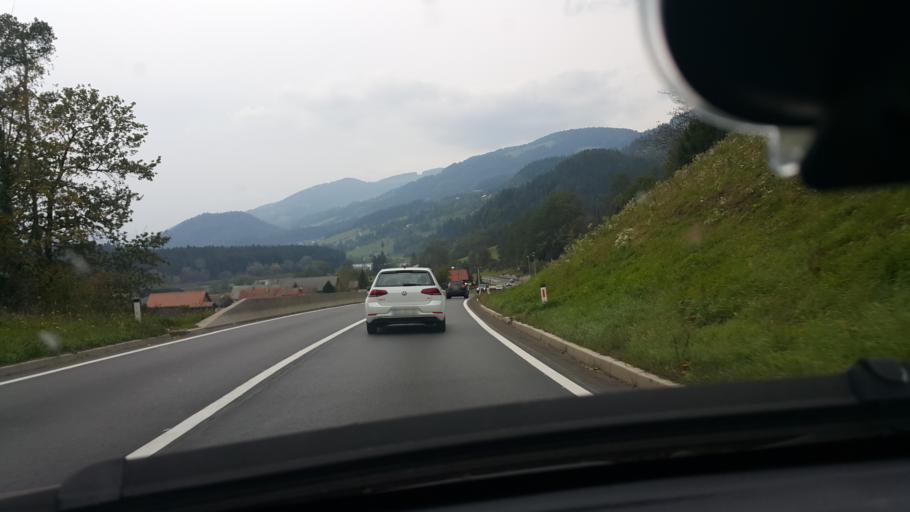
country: SI
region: Radlje ob Dravi
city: Radlje ob Dravi
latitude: 46.6142
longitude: 15.1995
